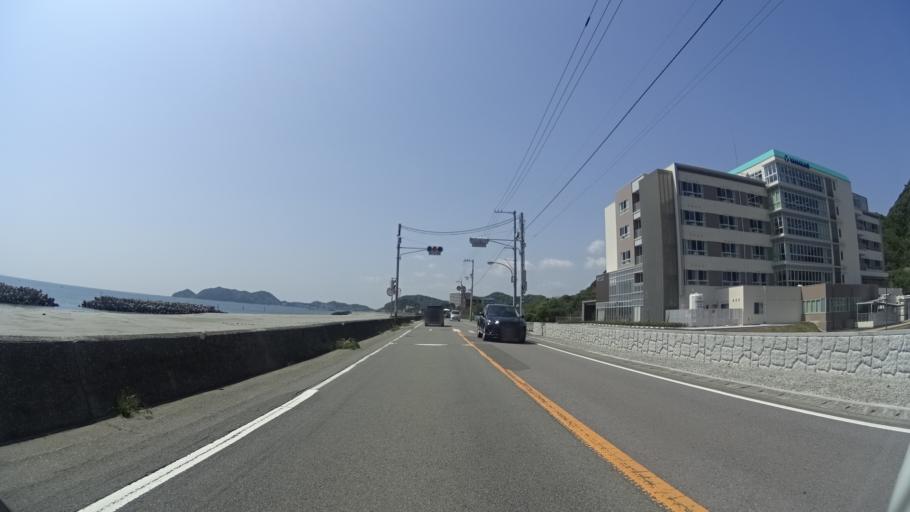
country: JP
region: Tokushima
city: Narutocho-mitsuishi
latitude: 34.2058
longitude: 134.6264
